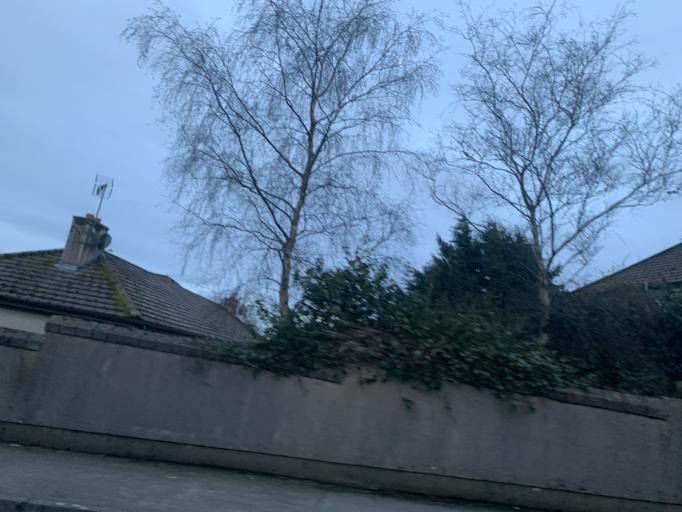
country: IE
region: Connaught
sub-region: Sligo
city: Collooney
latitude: 54.1803
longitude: -8.4922
